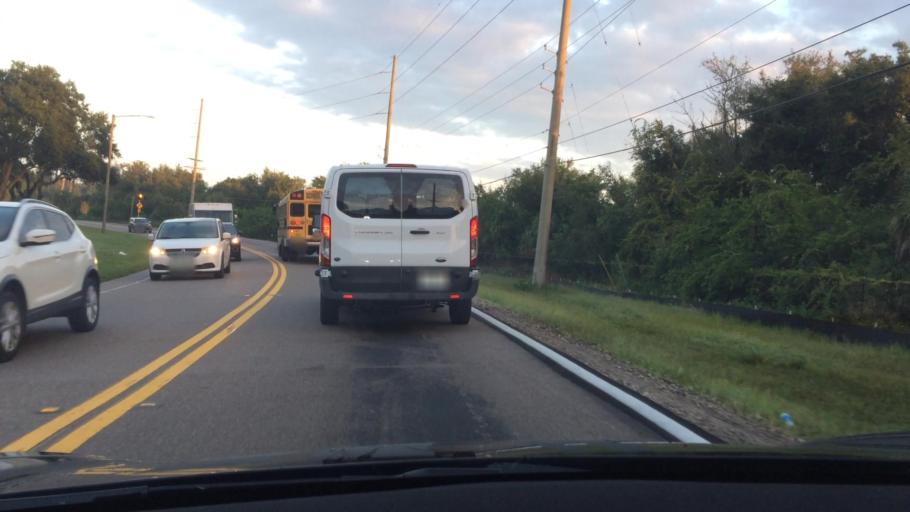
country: US
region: Florida
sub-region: Hillsborough County
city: Citrus Park
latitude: 28.0981
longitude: -82.5792
